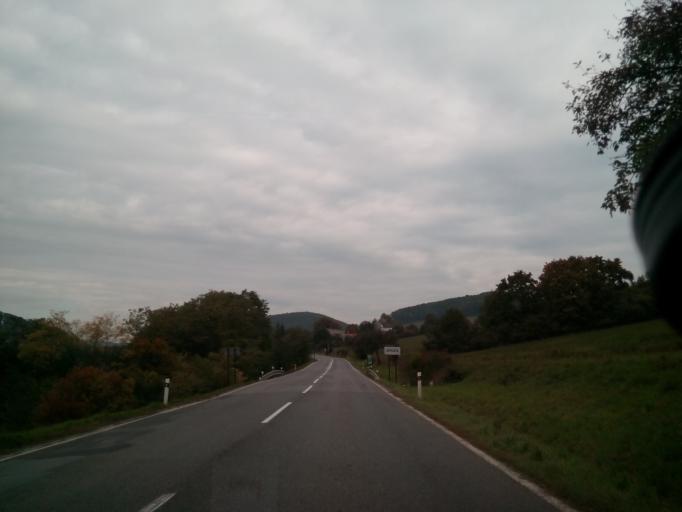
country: SK
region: Presovsky
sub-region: Okres Presov
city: Presov
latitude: 49.1017
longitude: 21.3149
